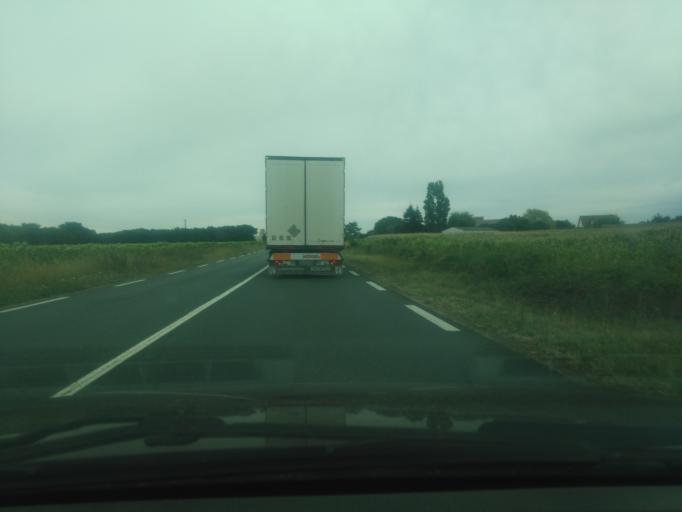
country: FR
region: Poitou-Charentes
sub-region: Departement de la Vienne
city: Lavoux
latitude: 46.5614
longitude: 0.5463
